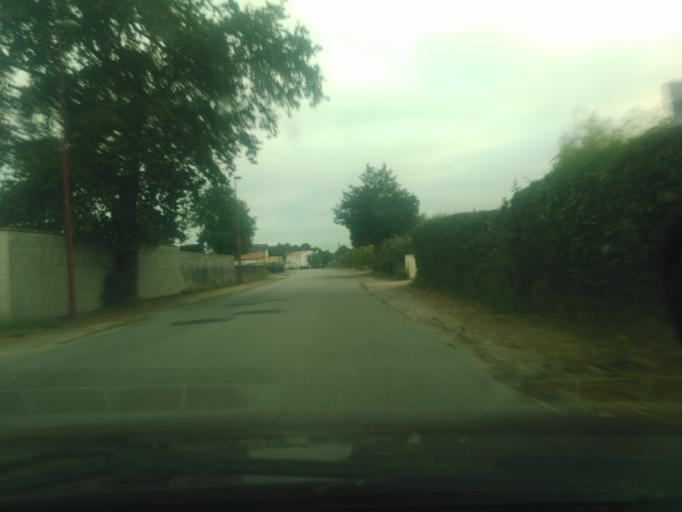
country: FR
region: Pays de la Loire
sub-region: Departement de la Vendee
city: Saint-Denis-la-Chevasse
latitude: 46.7917
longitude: -1.3178
